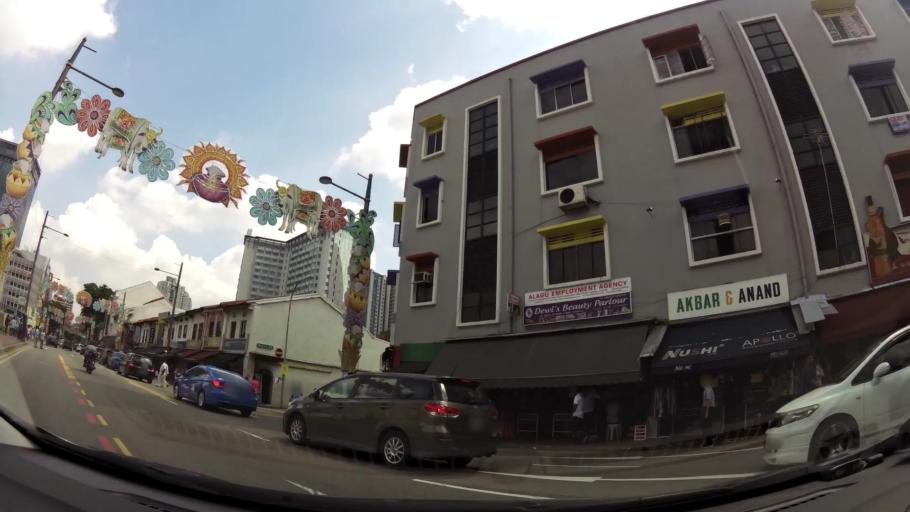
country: SG
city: Singapore
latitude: 1.3097
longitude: 103.8538
